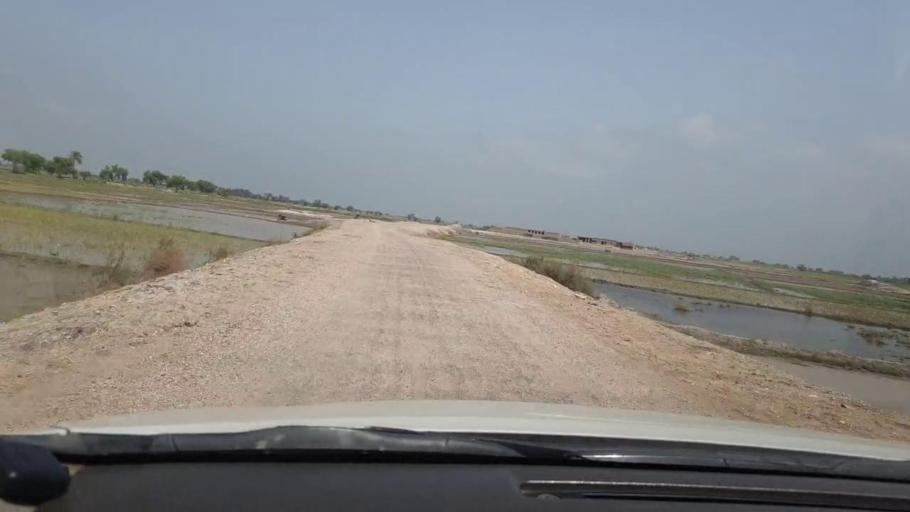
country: PK
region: Sindh
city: Shikarpur
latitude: 27.9999
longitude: 68.5596
